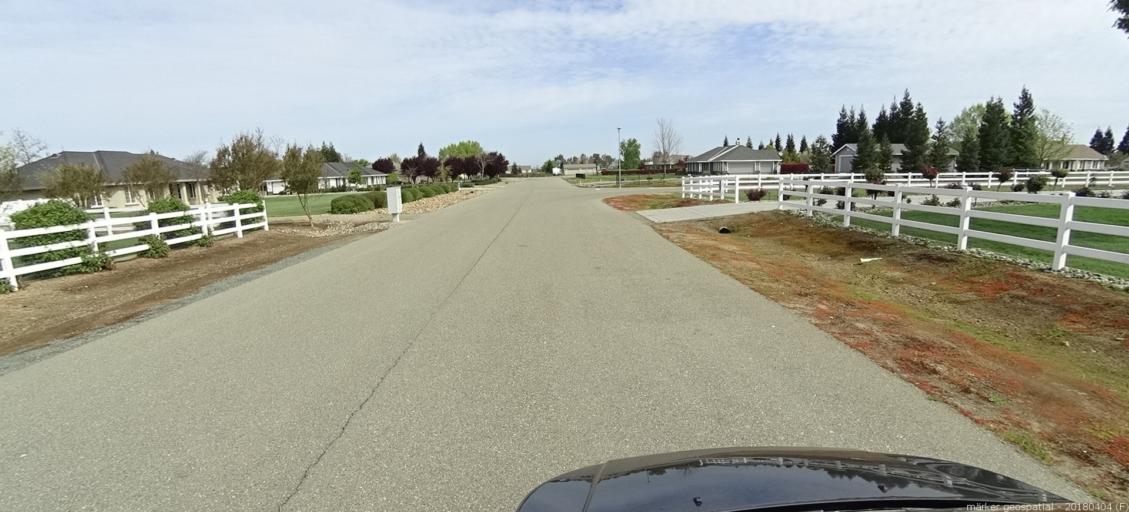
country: US
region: California
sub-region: Sacramento County
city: Galt
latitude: 38.2941
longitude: -121.2902
